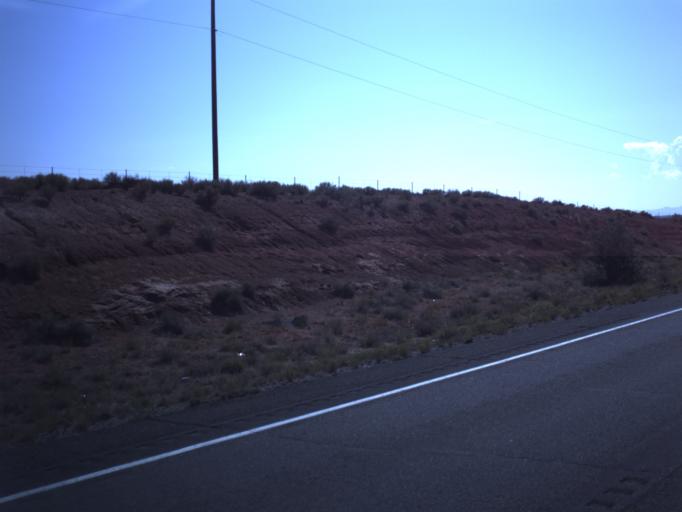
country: US
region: Utah
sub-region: San Juan County
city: Blanding
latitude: 37.1513
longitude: -109.5667
